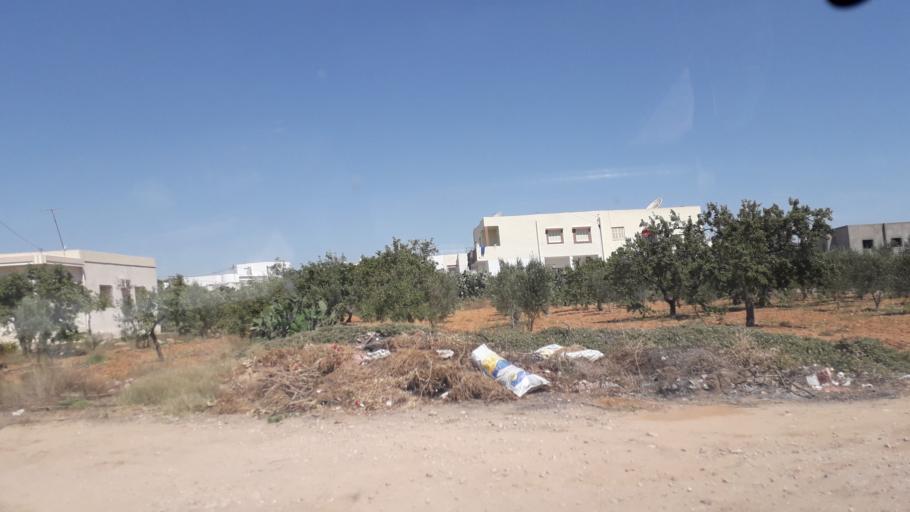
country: TN
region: Safaqis
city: Al Qarmadah
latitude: 34.8211
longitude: 10.7659
